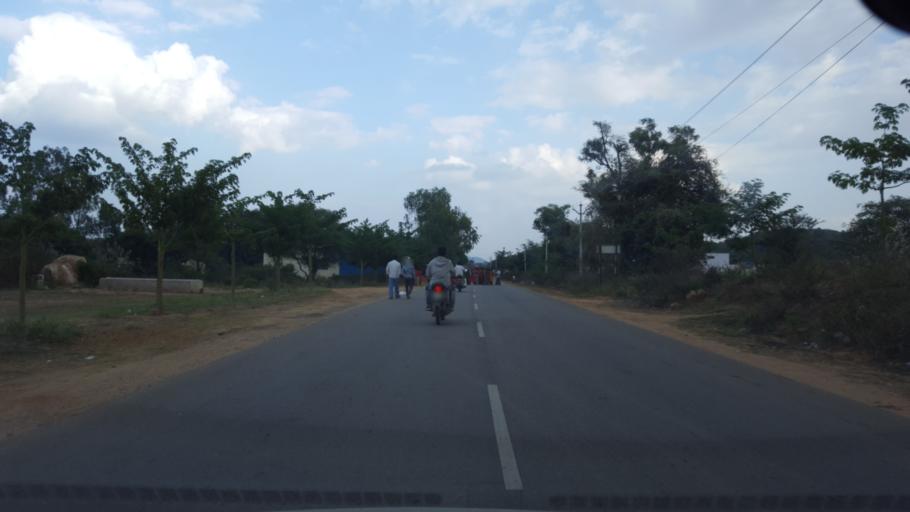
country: IN
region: Telangana
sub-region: Mahbubnagar
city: Mahbubnagar
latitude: 16.7598
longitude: 77.9588
